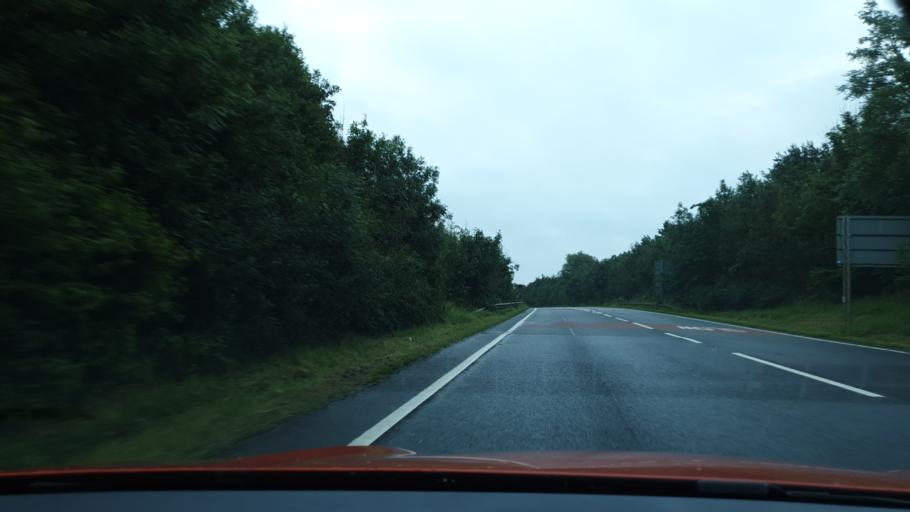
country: GB
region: England
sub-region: Cumbria
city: Dalton in Furness
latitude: 54.1637
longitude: -3.1872
